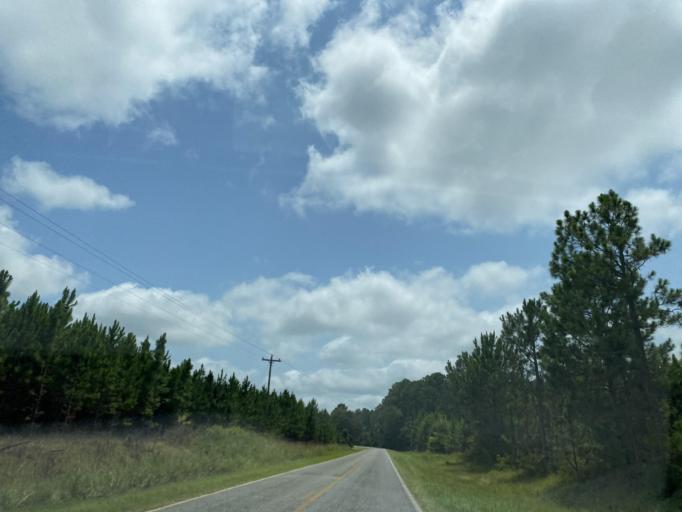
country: US
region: Georgia
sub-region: Wheeler County
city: Alamo
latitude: 32.1055
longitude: -82.7730
